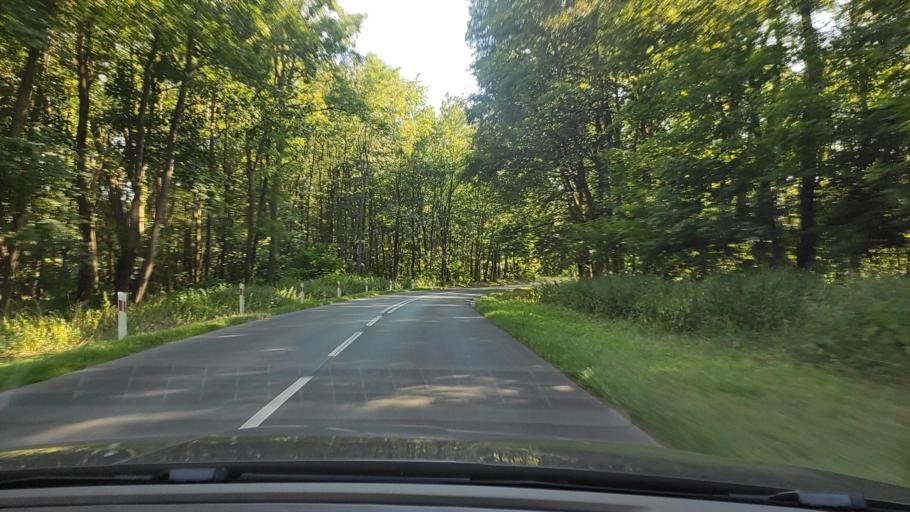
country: PL
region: Greater Poland Voivodeship
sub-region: Powiat poznanski
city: Kobylnica
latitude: 52.4563
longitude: 17.0872
